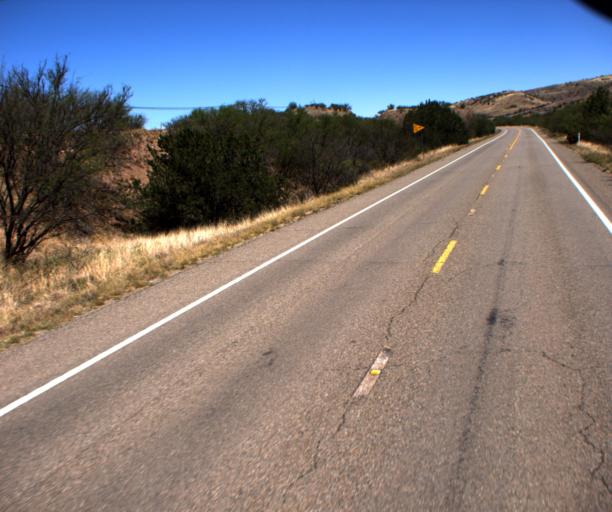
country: US
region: Arizona
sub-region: Santa Cruz County
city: Rio Rico
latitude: 31.6308
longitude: -110.7142
